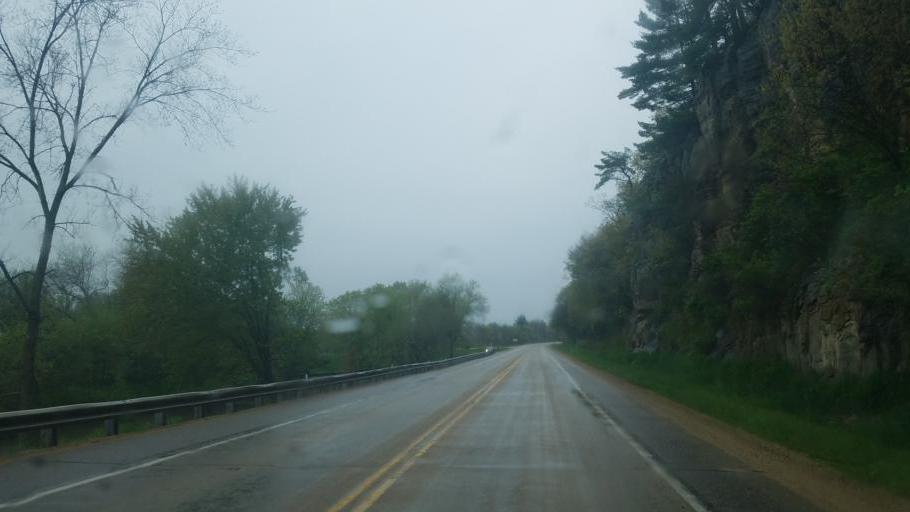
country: US
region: Wisconsin
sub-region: Juneau County
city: Elroy
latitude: 43.6401
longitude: -90.2088
